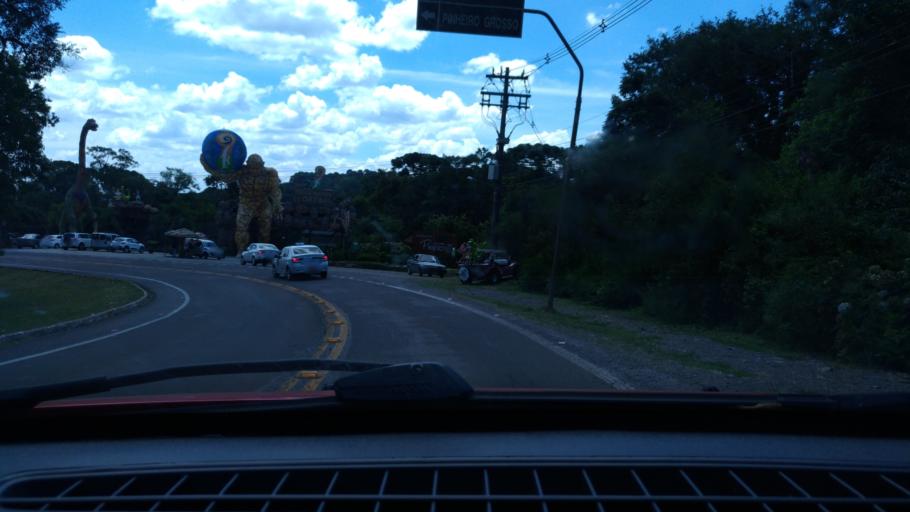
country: BR
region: Rio Grande do Sul
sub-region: Canela
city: Canela
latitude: -29.3500
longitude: -50.8322
